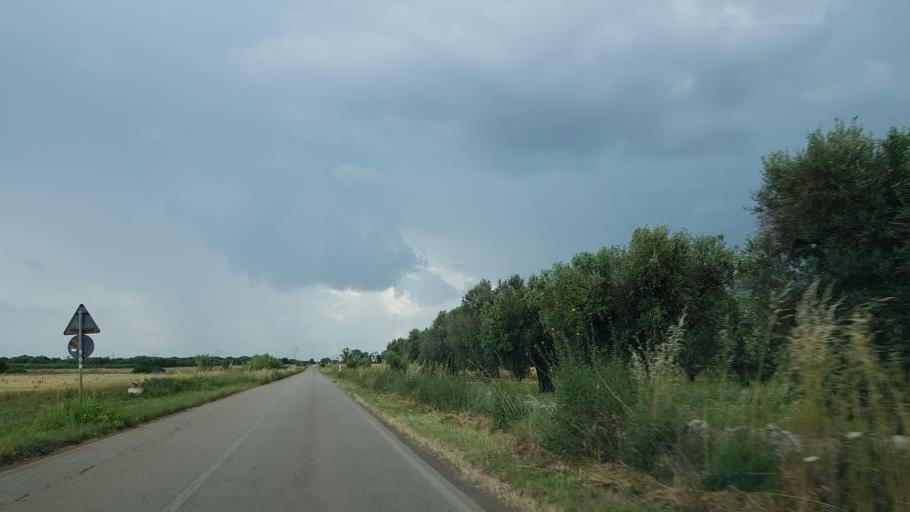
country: IT
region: Apulia
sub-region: Provincia di Lecce
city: Porto Cesareo
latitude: 40.3306
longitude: 17.8524
